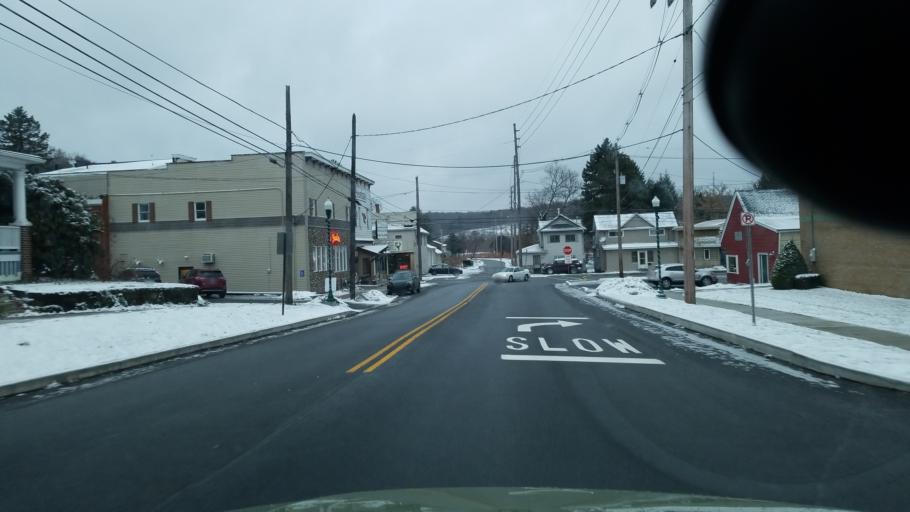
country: US
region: Pennsylvania
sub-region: Clearfield County
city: DuBois
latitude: 41.1237
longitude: -78.7677
